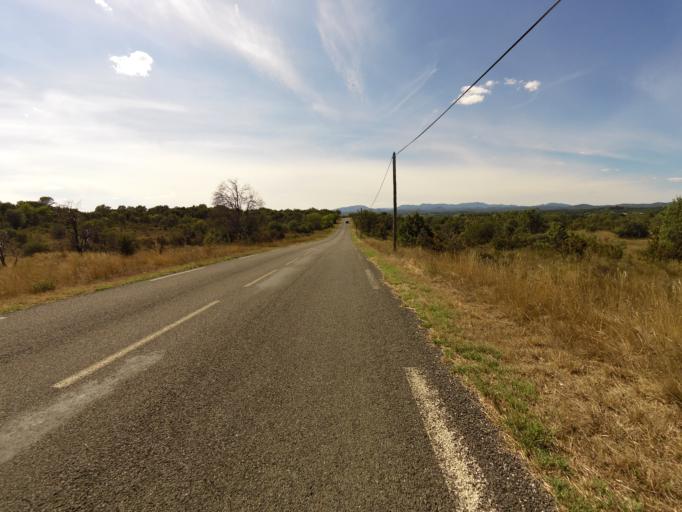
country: FR
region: Languedoc-Roussillon
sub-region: Departement du Gard
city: Lezan
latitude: 43.9591
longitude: 4.0447
